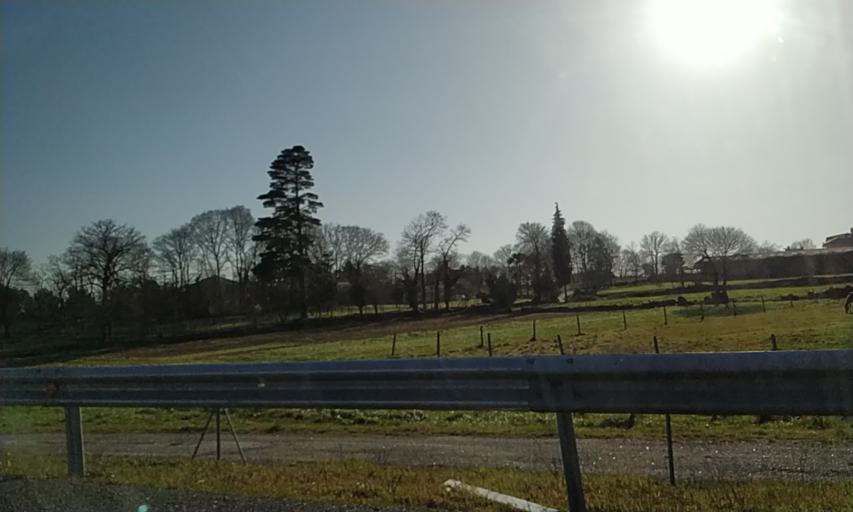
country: ES
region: Galicia
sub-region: Provincia de Lugo
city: Outeiro de Rei
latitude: 43.0793
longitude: -7.5792
